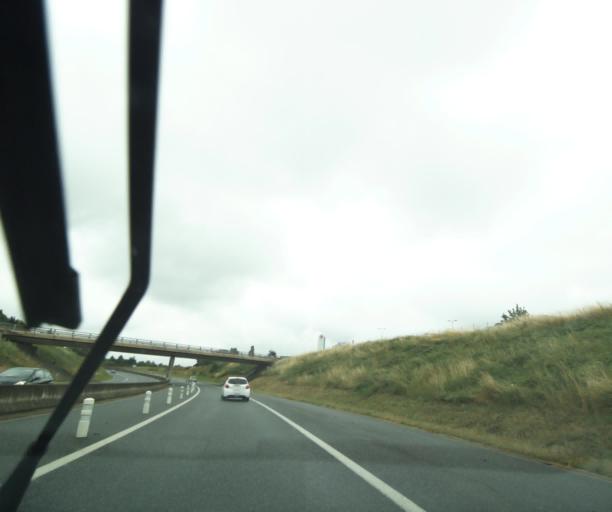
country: FR
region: Midi-Pyrenees
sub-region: Departement de l'Aveyron
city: Olemps
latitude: 44.3250
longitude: 2.5566
